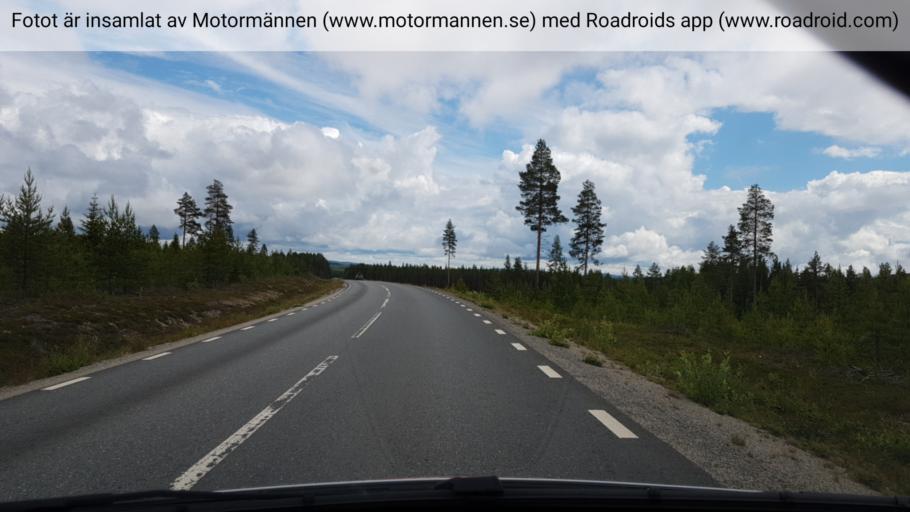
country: SE
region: Vaesterbotten
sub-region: Lycksele Kommun
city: Lycksele
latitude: 64.3932
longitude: 19.0762
